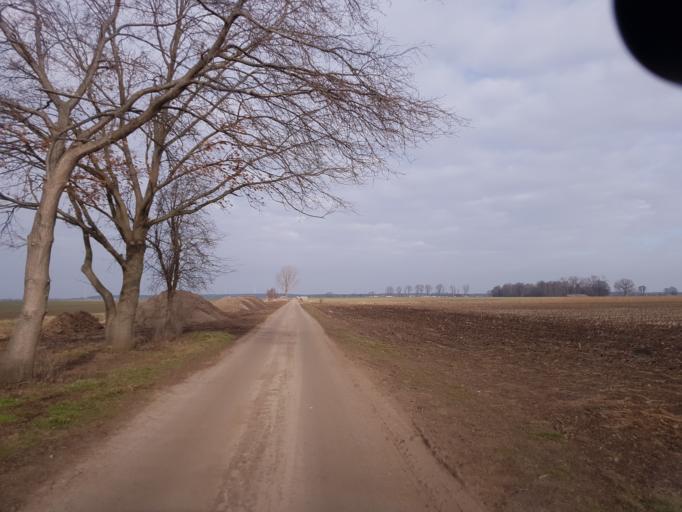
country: DE
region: Brandenburg
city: Doberlug-Kirchhain
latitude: 51.6622
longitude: 13.5428
